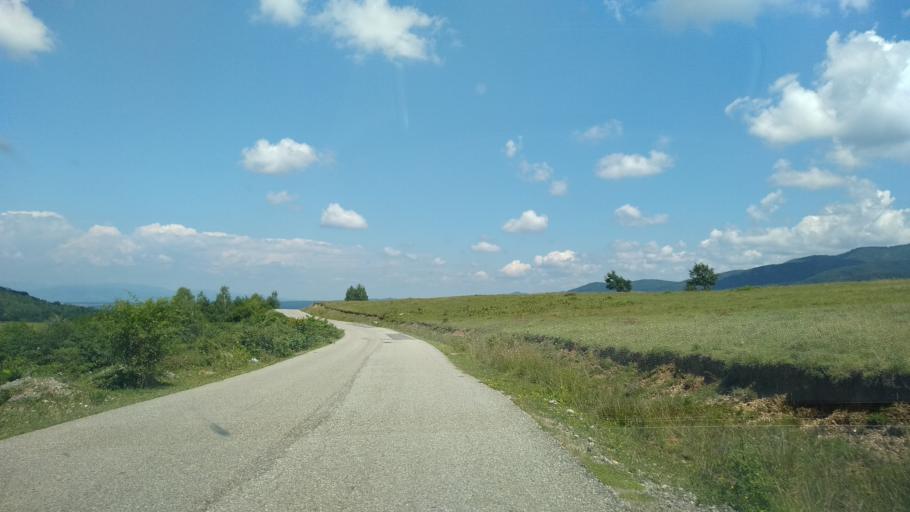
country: RO
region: Hunedoara
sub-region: Comuna Orastioara de Sus
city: Orastioara de Sus
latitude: 45.7123
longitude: 23.1544
